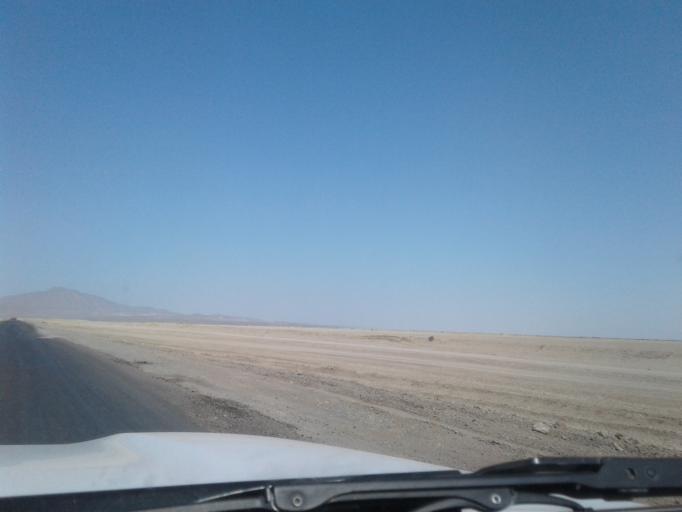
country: TM
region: Balkan
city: Gumdag
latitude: 39.2226
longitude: 54.6630
